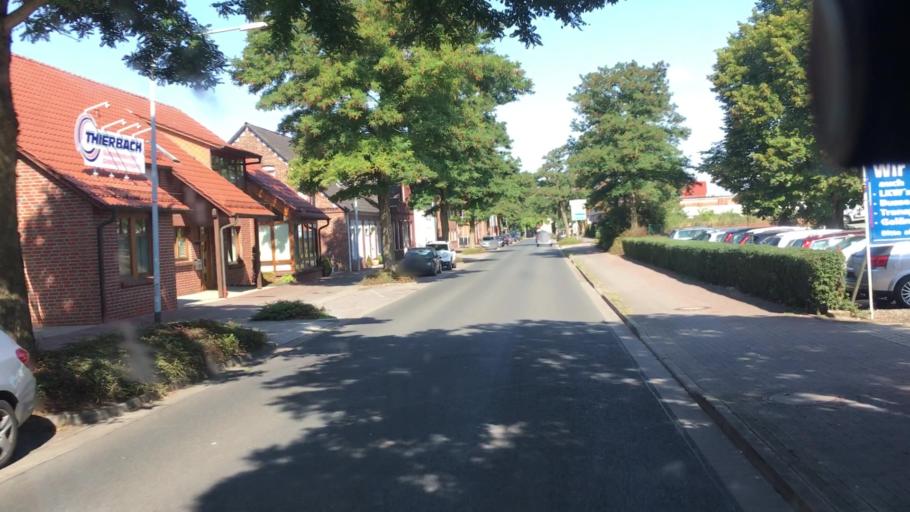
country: DE
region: Lower Saxony
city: Lohne
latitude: 52.6574
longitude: 8.2407
